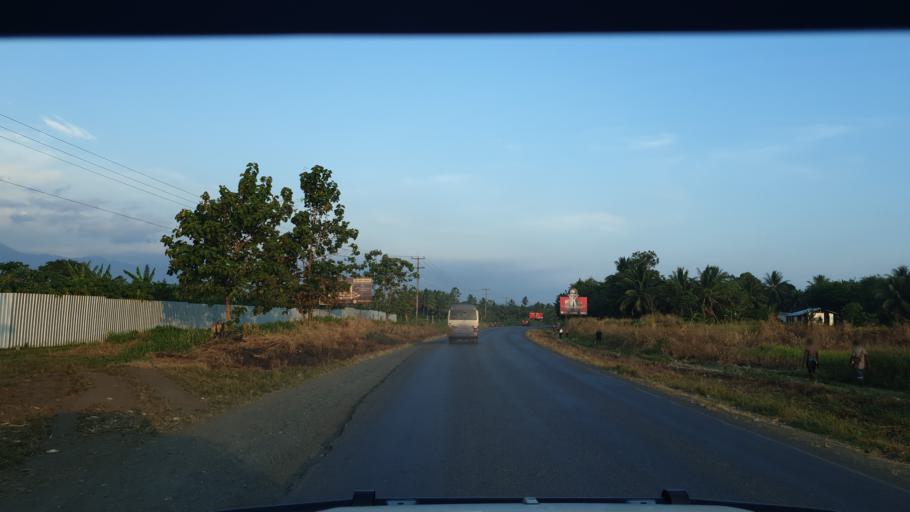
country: PG
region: Morobe
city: Lae
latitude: -6.5644
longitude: 146.7549
